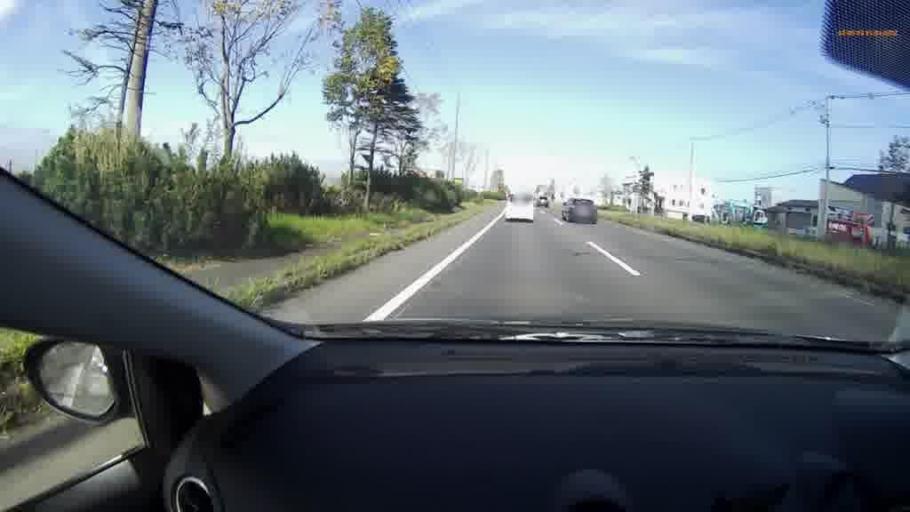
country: JP
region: Hokkaido
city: Kushiro
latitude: 43.0052
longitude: 144.4164
